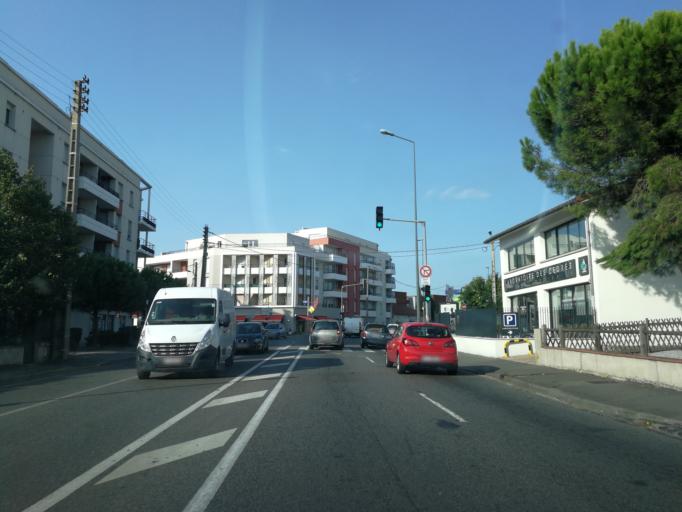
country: FR
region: Midi-Pyrenees
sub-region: Departement de la Haute-Garonne
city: Toulouse
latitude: 43.6221
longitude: 1.4253
